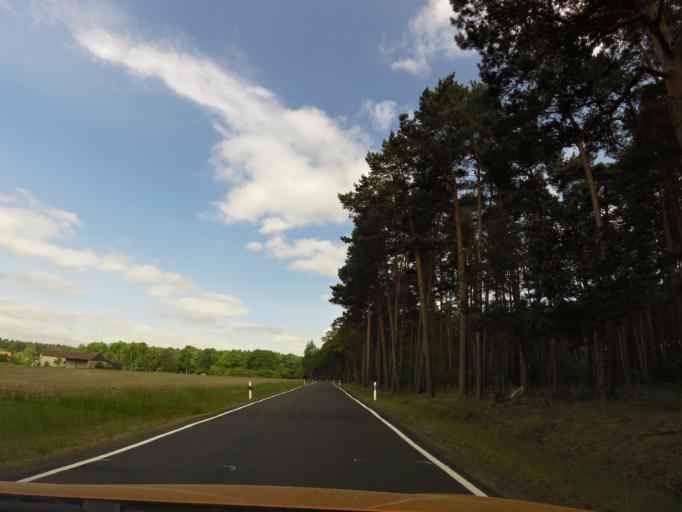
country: DE
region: Brandenburg
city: Wiesenburg
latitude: 52.0804
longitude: 12.5048
